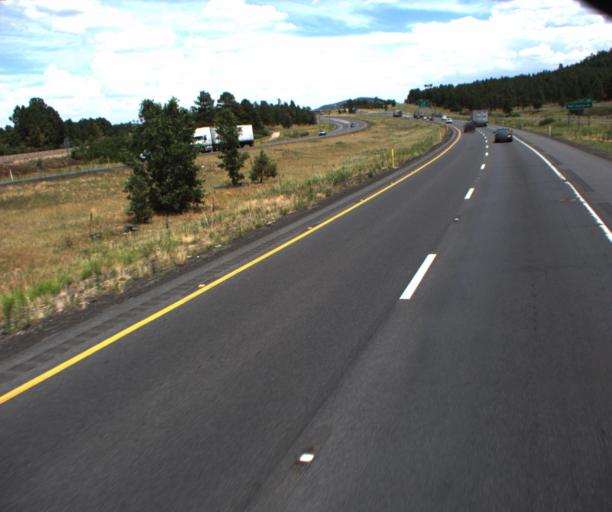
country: US
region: Arizona
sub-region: Coconino County
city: Williams
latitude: 35.2375
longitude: -112.2218
